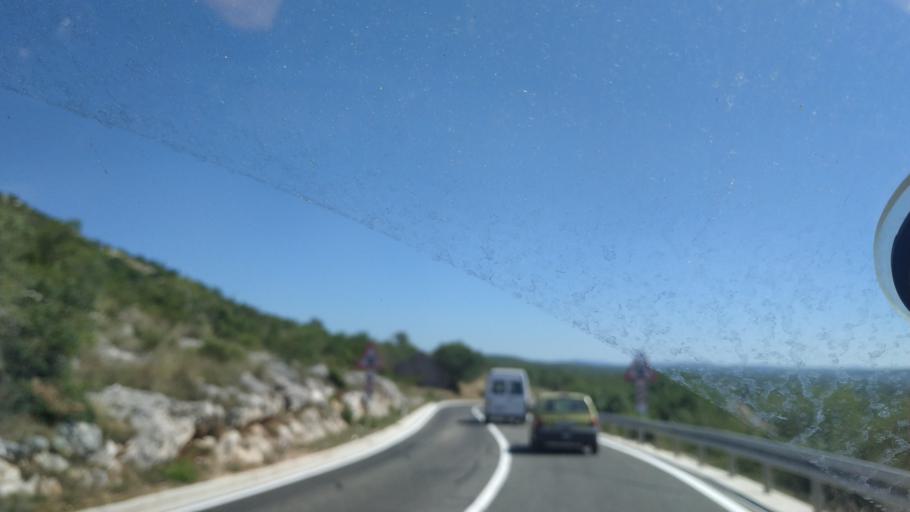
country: HR
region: Sibensko-Kniniska
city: Drnis
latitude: 43.8454
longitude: 16.1469
